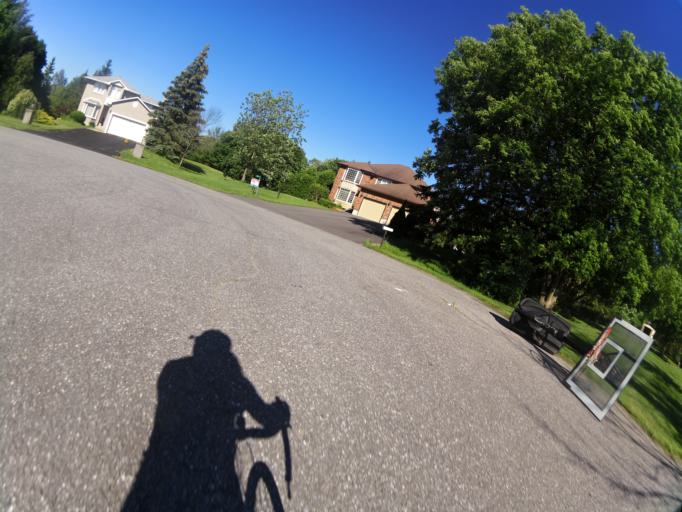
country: CA
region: Ontario
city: Bells Corners
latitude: 45.2626
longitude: -75.8212
